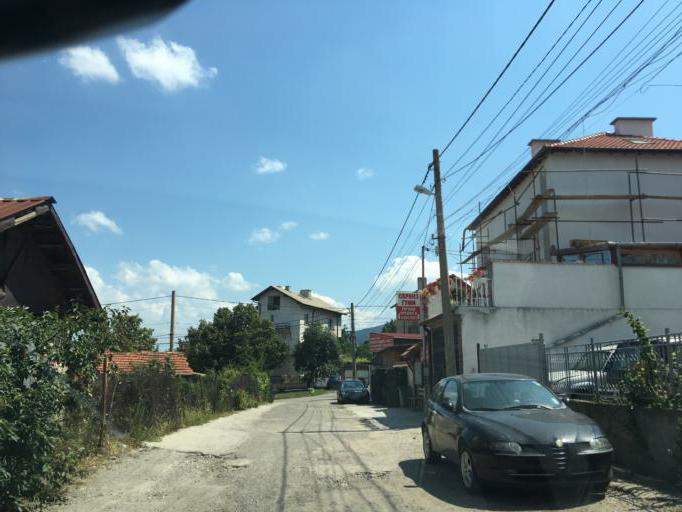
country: BG
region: Sofiya
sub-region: Obshtina Elin Pelin
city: Elin Pelin
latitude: 42.6027
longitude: 23.4717
